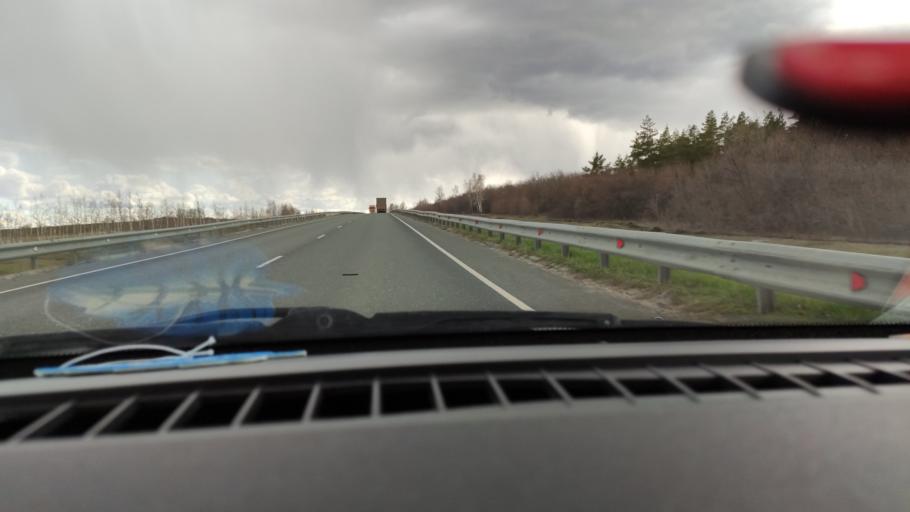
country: RU
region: Saratov
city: Balakovo
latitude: 52.1690
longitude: 47.8283
